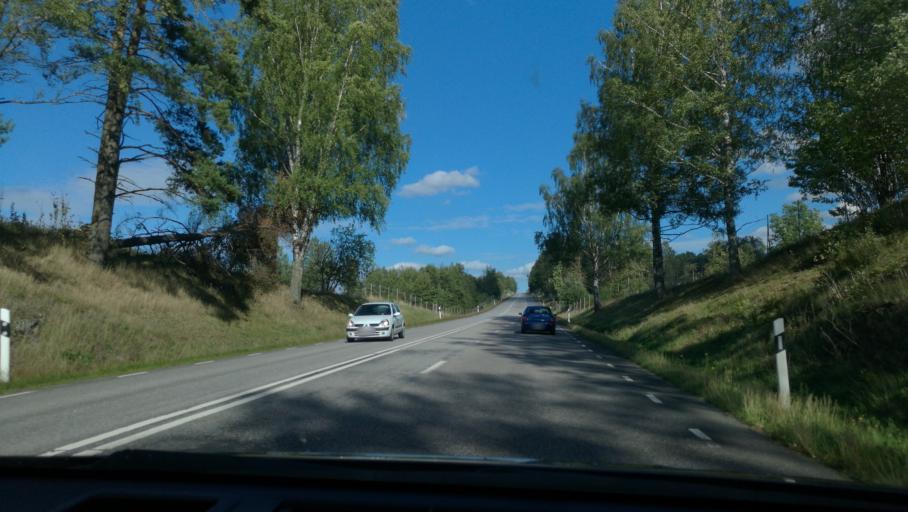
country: SE
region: Vaestra Goetaland
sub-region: Gullspangs Kommun
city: Anderstorp
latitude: 58.8726
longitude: 14.2505
